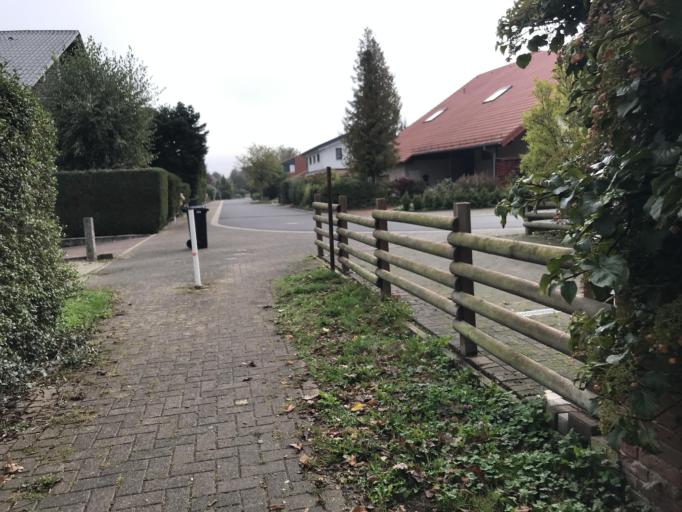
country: DE
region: Hesse
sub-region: Regierungsbezirk Kassel
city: Baunatal
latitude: 51.2050
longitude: 9.4300
